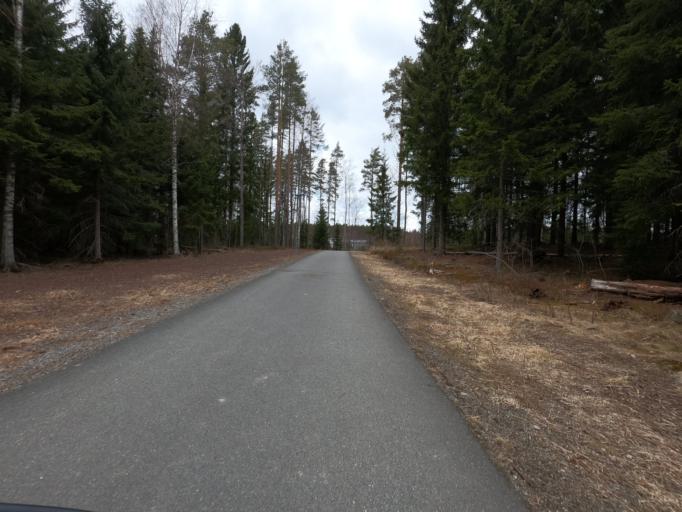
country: FI
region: North Karelia
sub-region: Joensuu
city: Joensuu
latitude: 62.5694
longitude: 29.8134
